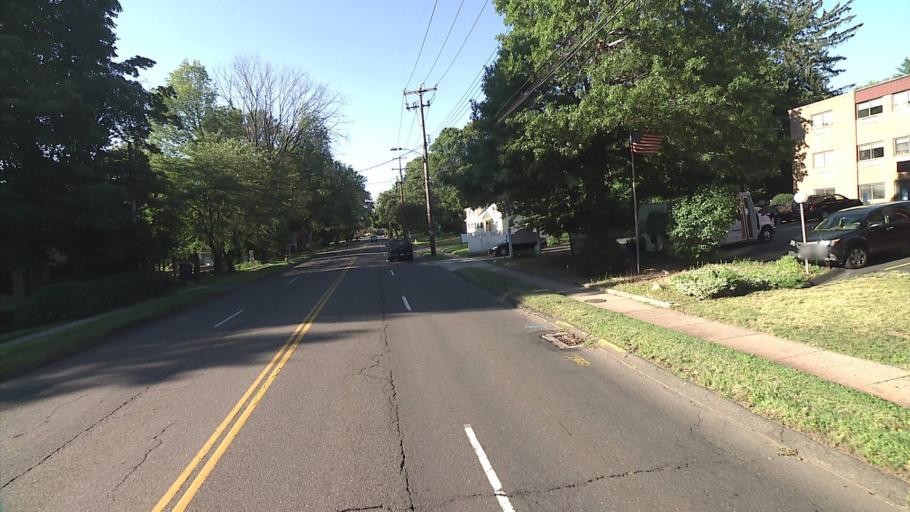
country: US
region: Connecticut
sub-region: New Haven County
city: Hamden
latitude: 41.3979
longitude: -72.8973
